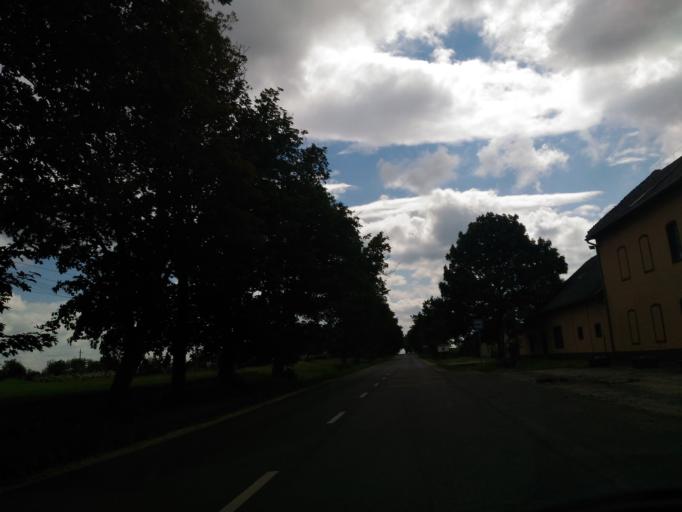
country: HU
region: Fejer
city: Pusztaszabolcs
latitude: 47.1363
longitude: 18.7764
